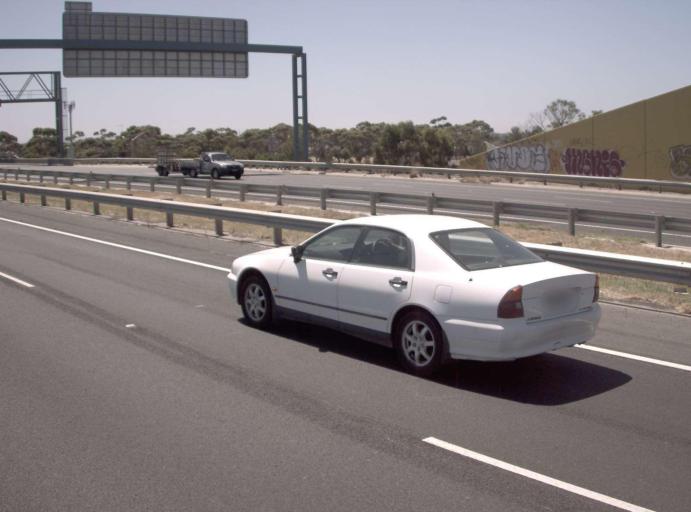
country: AU
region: Victoria
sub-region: Brimbank
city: Deer Park
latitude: -37.7828
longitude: 144.7904
